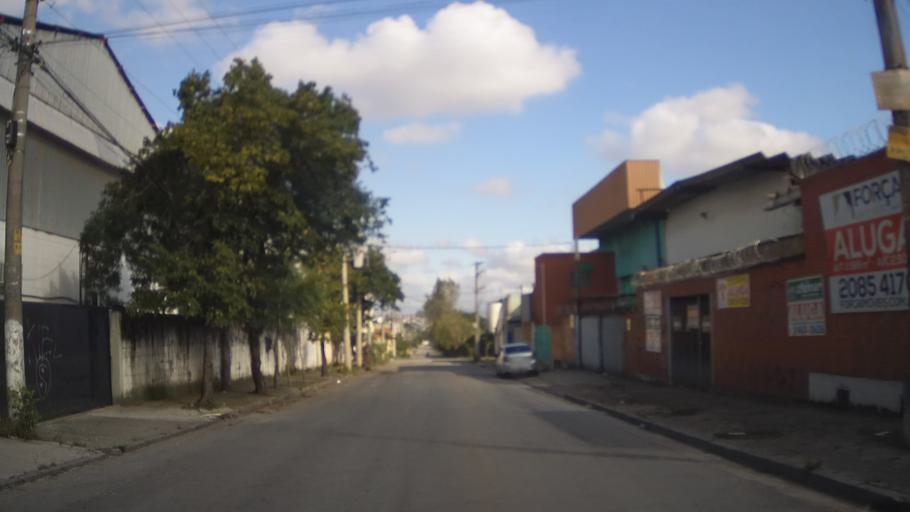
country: BR
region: Sao Paulo
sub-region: Guarulhos
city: Guarulhos
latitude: -23.4601
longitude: -46.4722
